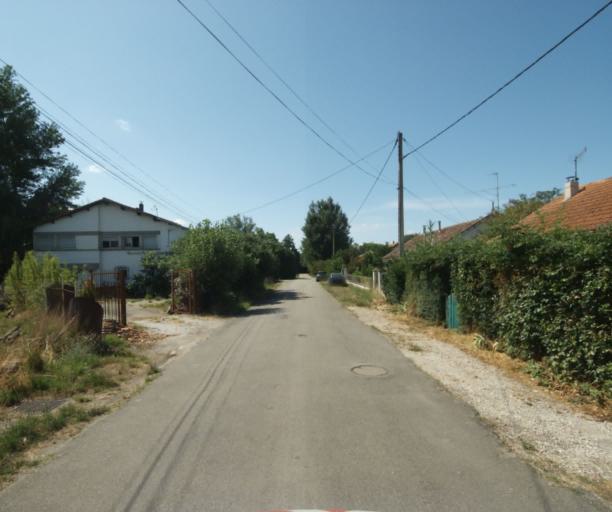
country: FR
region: Midi-Pyrenees
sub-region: Departement de la Haute-Garonne
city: Revel
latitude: 43.4703
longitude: 2.0110
